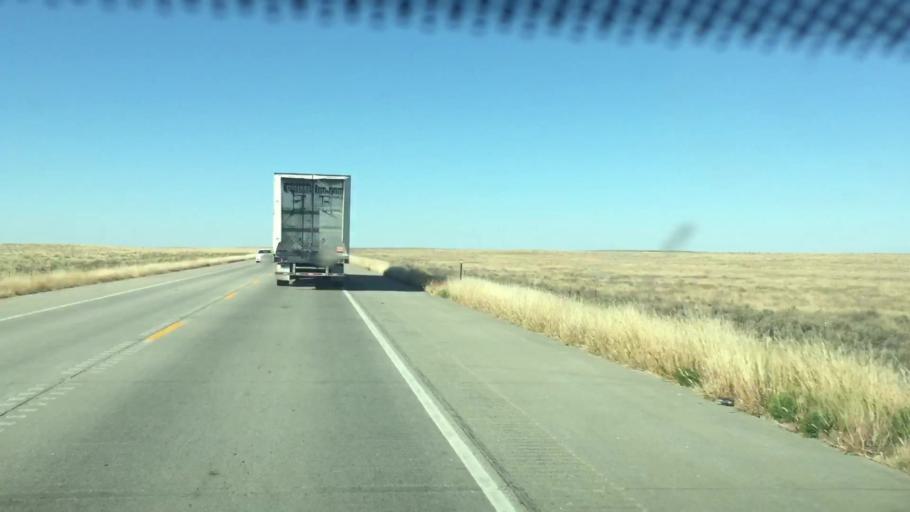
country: US
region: Colorado
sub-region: Kiowa County
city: Eads
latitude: 38.5138
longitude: -102.7856
